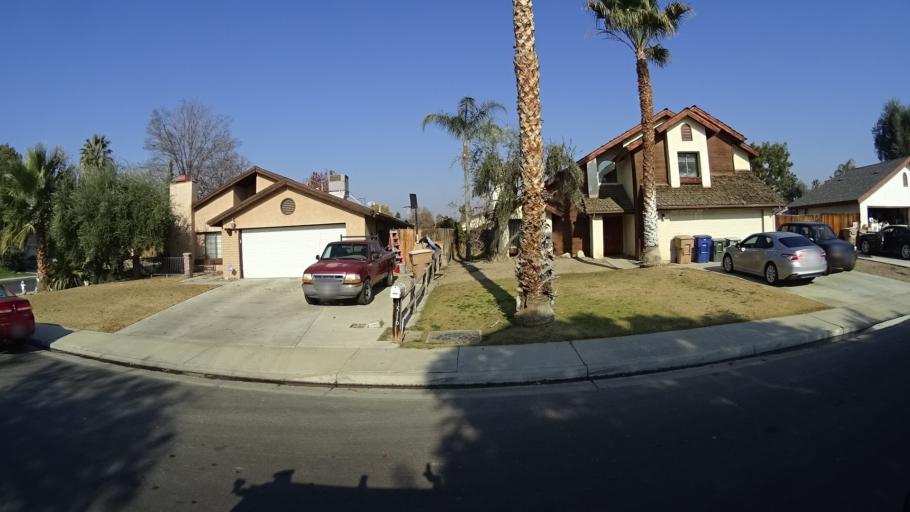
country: US
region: California
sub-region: Kern County
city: Greenacres
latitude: 35.3202
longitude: -119.0861
